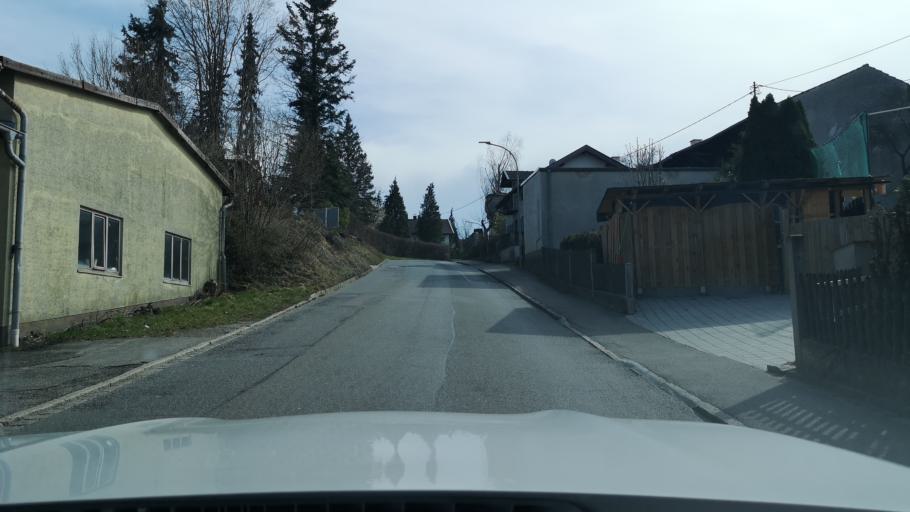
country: DE
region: Bavaria
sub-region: Upper Bavaria
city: Isen
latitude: 48.2099
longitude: 12.0554
